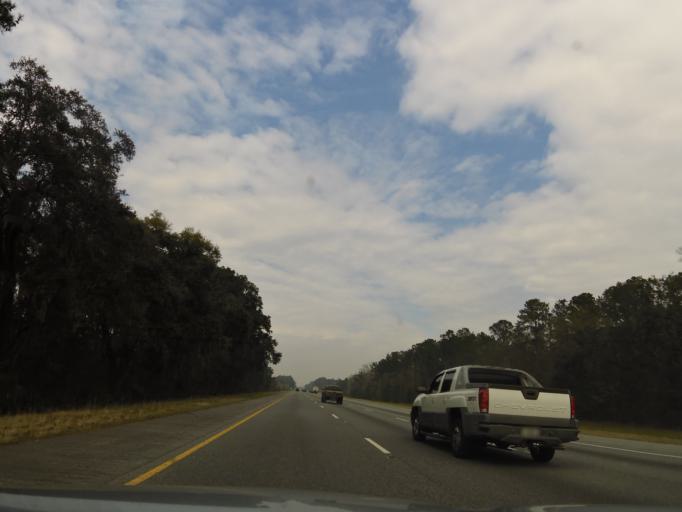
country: US
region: Georgia
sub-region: Liberty County
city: Midway
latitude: 31.7102
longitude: -81.3900
